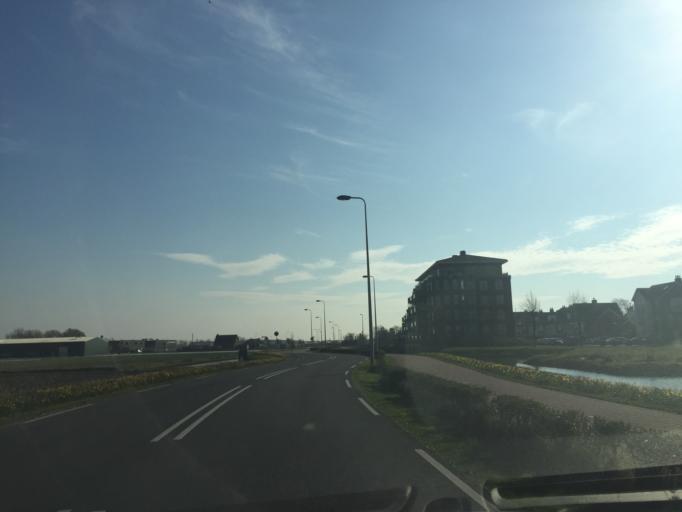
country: NL
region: South Holland
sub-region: Gemeente Noordwijkerhout
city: Noordwijkerhout
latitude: 52.2620
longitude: 4.5054
